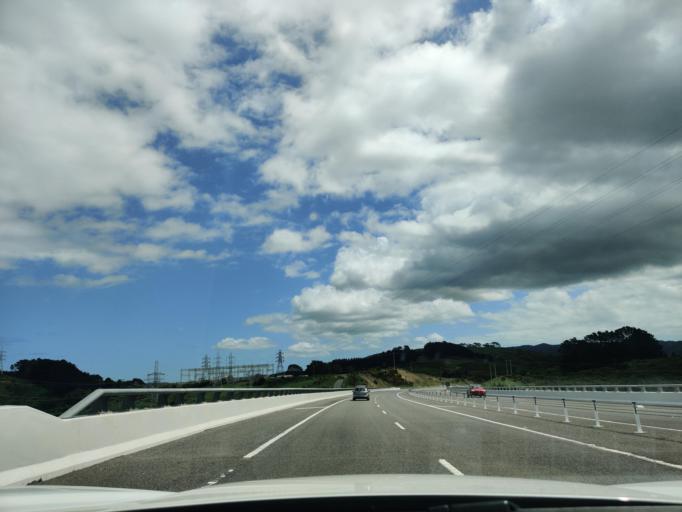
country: NZ
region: Wellington
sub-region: Porirua City
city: Porirua
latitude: -41.1552
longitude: 174.8763
